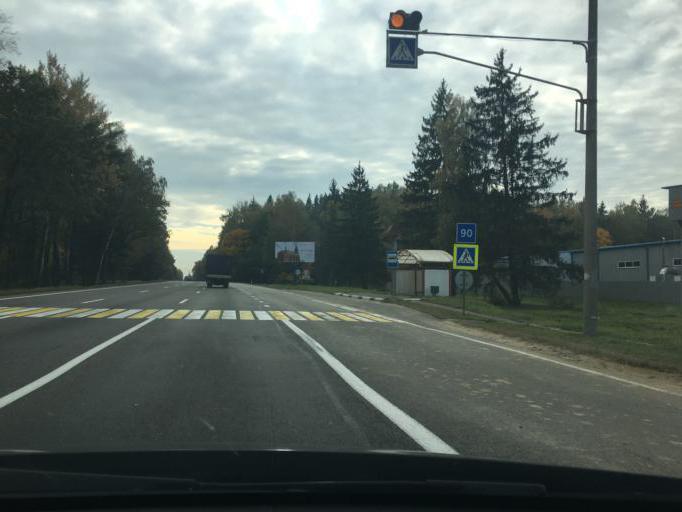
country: BY
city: Fanipol
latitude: 53.7908
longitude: 27.3659
